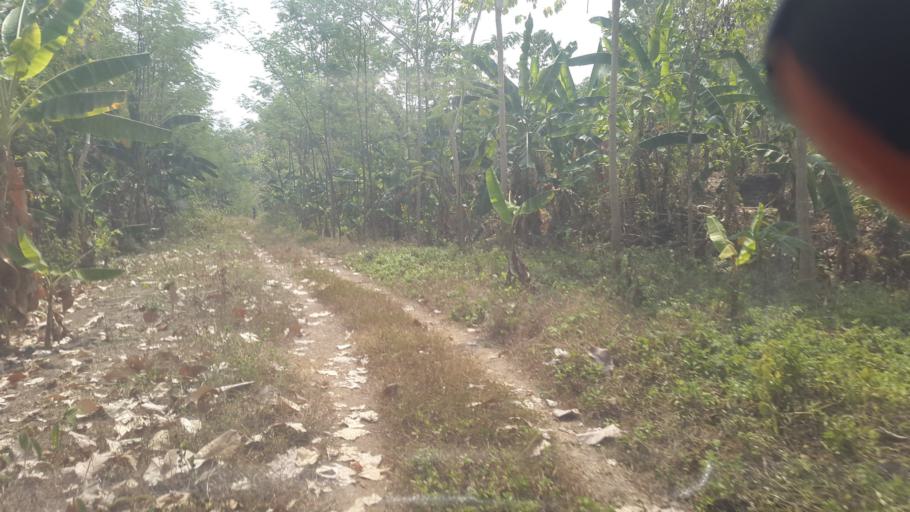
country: ID
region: West Java
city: Cimaja
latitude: -6.9476
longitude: 106.5061
